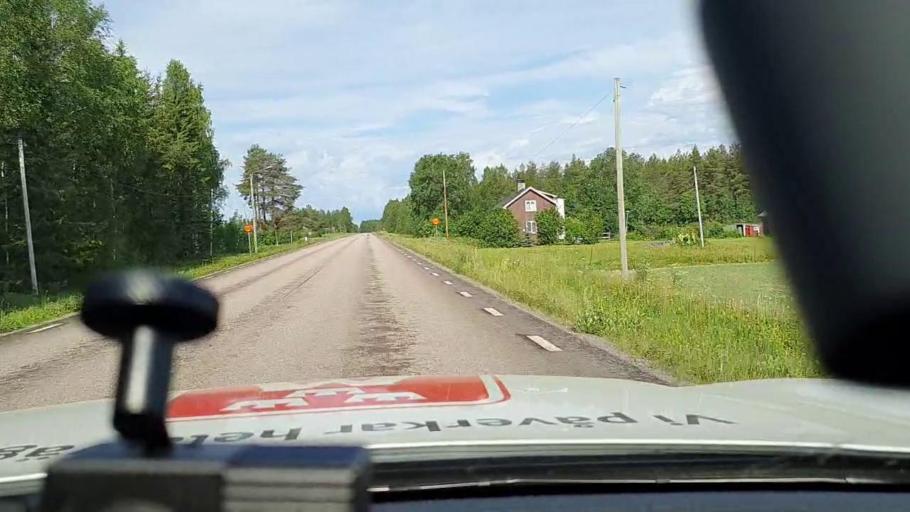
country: SE
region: Norrbotten
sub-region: Alvsbyns Kommun
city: AElvsbyn
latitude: 66.0176
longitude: 21.1504
